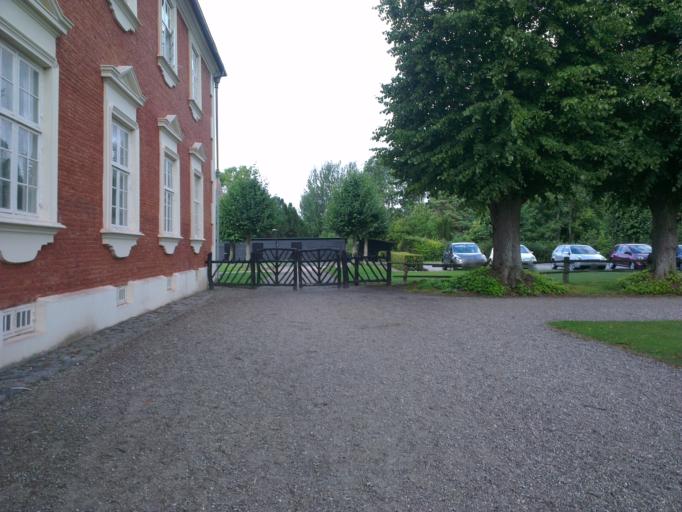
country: DK
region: Capital Region
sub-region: Frederikssund Kommune
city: Jaegerspris
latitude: 55.8567
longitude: 11.9741
